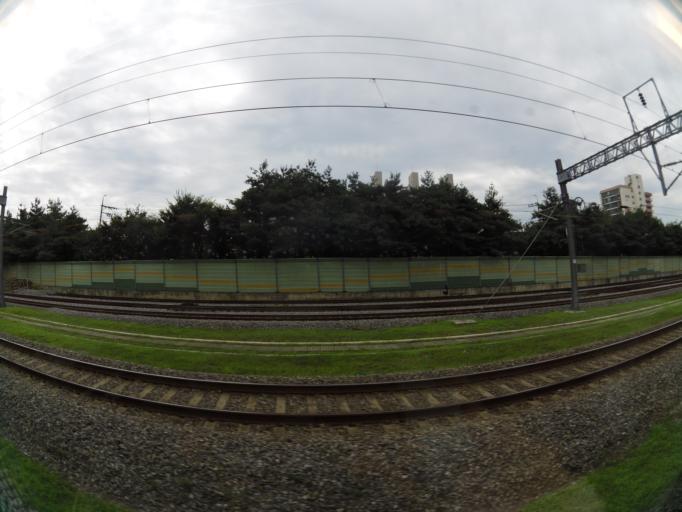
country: KR
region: Chungcheongnam-do
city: Seonghwan
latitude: 36.9878
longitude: 127.0882
